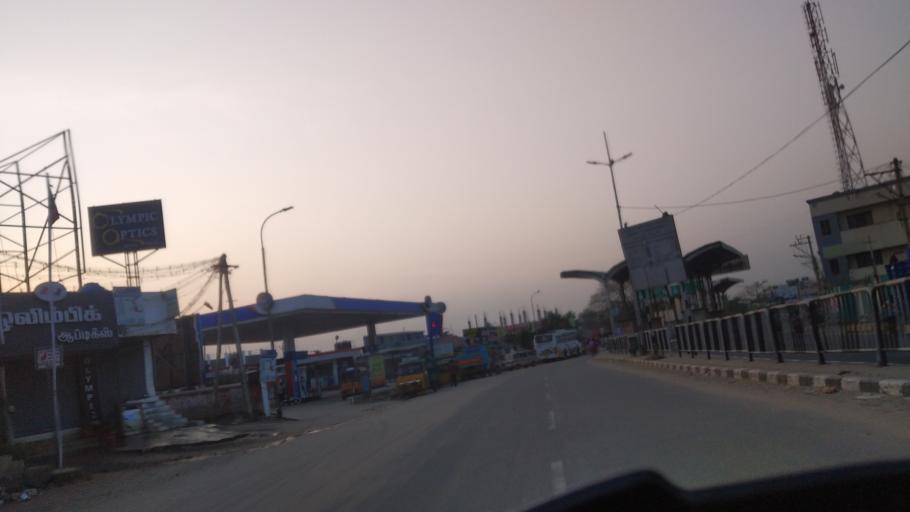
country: IN
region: Tamil Nadu
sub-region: Coimbatore
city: Coimbatore
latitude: 10.9768
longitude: 76.9615
